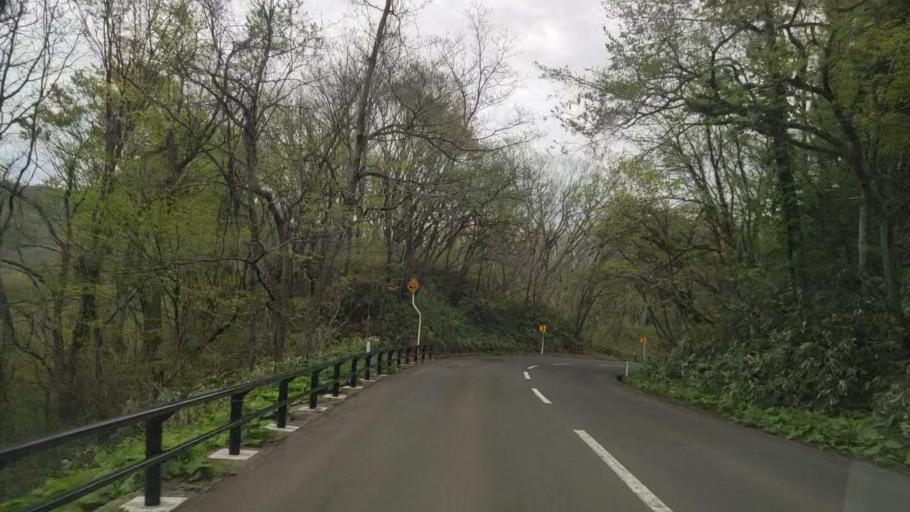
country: JP
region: Akita
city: Hanawa
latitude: 40.3738
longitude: 140.7902
